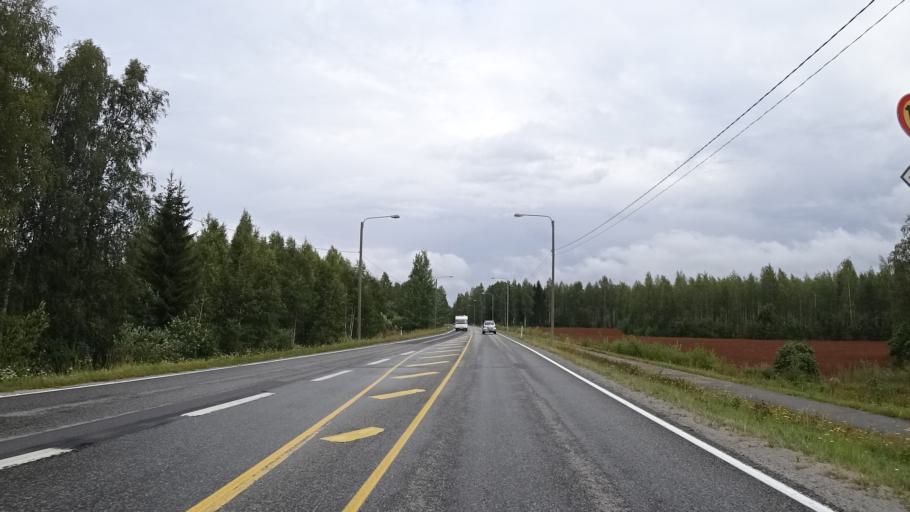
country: FI
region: Southern Savonia
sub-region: Savonlinna
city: Kerimaeki
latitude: 61.9271
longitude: 29.2711
